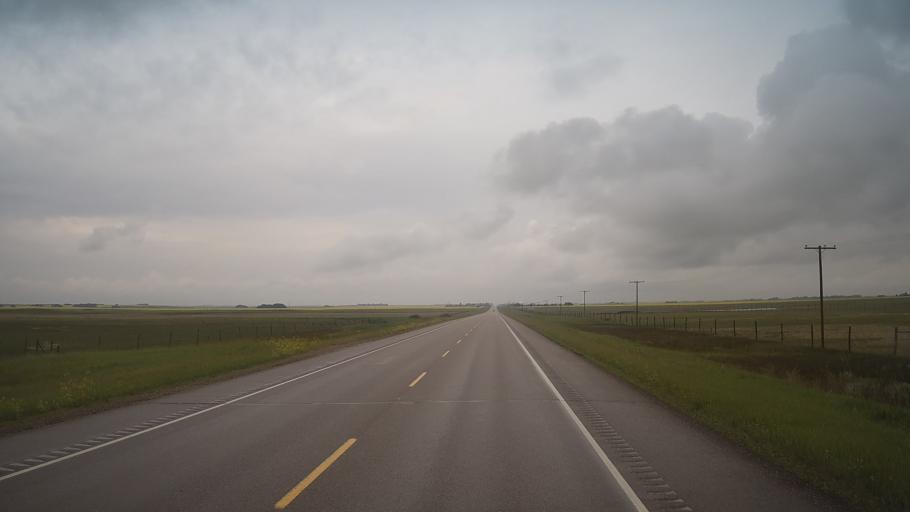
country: CA
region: Saskatchewan
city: Unity
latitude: 52.4349
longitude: -108.9868
